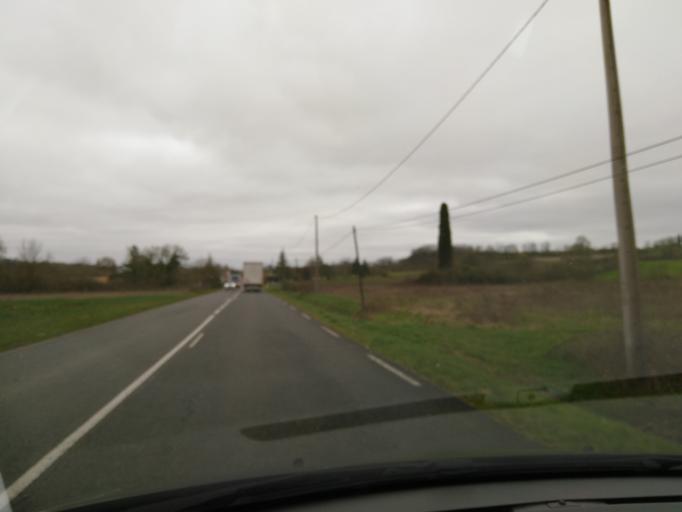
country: FR
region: Aquitaine
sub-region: Departement du Lot-et-Garonne
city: Castillonnes
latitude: 44.7100
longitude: 0.5603
